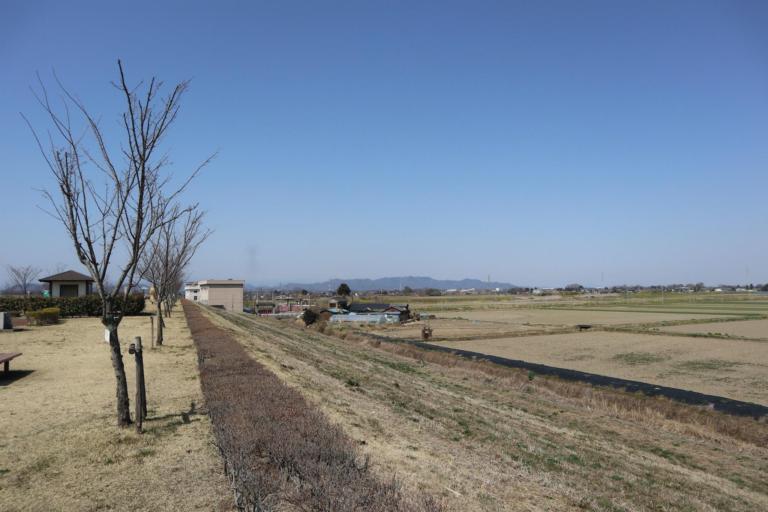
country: JP
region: Tochigi
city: Fujioka
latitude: 36.2450
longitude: 139.7015
